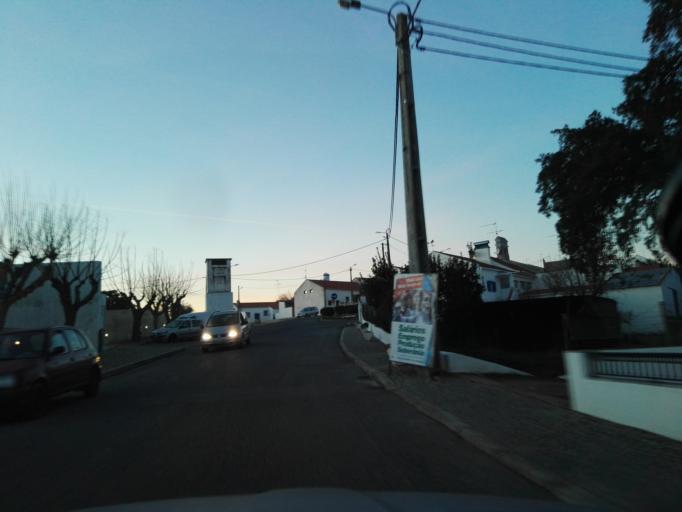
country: PT
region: Evora
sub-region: Arraiolos
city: Arraiolos
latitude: 38.7402
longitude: -8.0758
